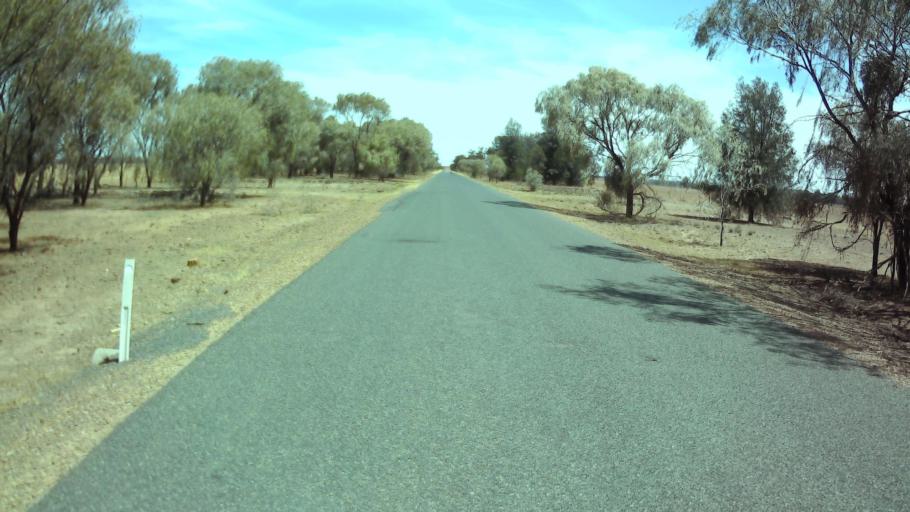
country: AU
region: New South Wales
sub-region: Weddin
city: Grenfell
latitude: -33.8759
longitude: 147.7438
